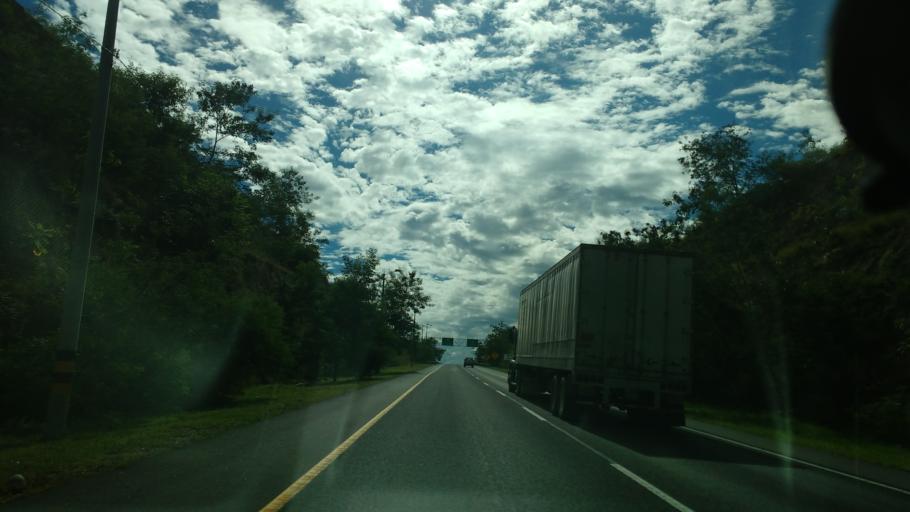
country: CO
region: Tolima
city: Valle de San Juan
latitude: 4.2939
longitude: -75.0419
